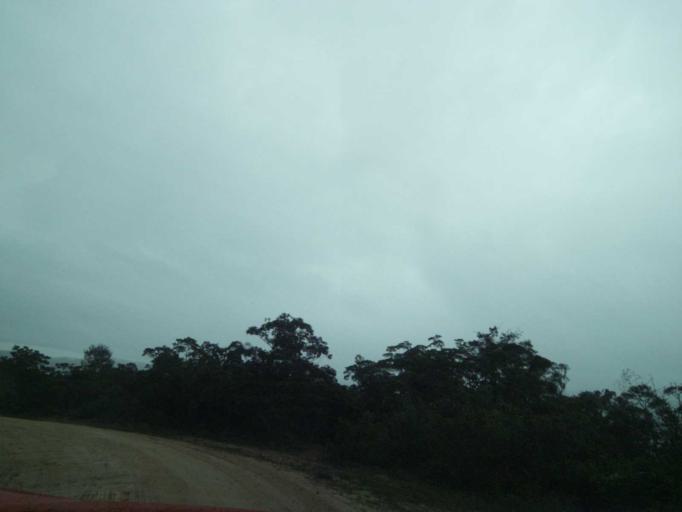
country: BR
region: Santa Catarina
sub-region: Anitapolis
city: Anitapolis
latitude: -27.9209
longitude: -49.1792
